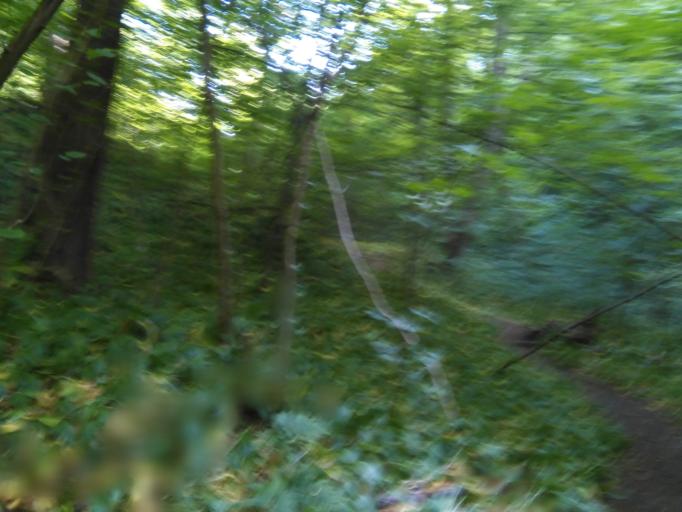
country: DK
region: Capital Region
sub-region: Bornholm Kommune
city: Akirkeby
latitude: 55.2239
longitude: 14.8803
